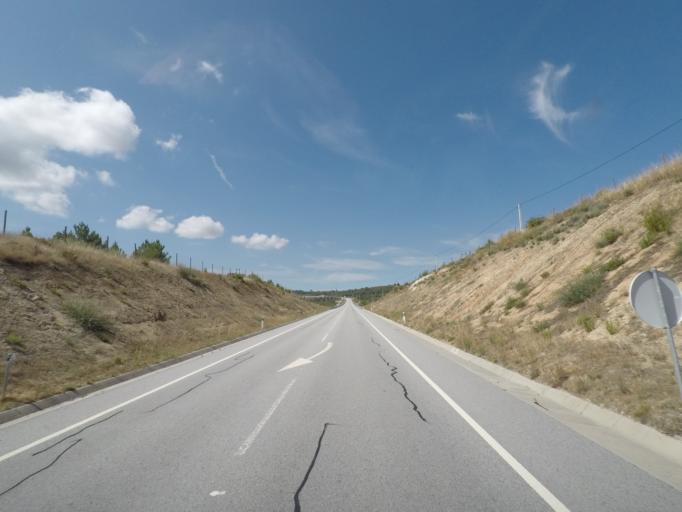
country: PT
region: Braganca
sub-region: Braganca Municipality
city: Vila Flor
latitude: 41.2677
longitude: -7.2158
